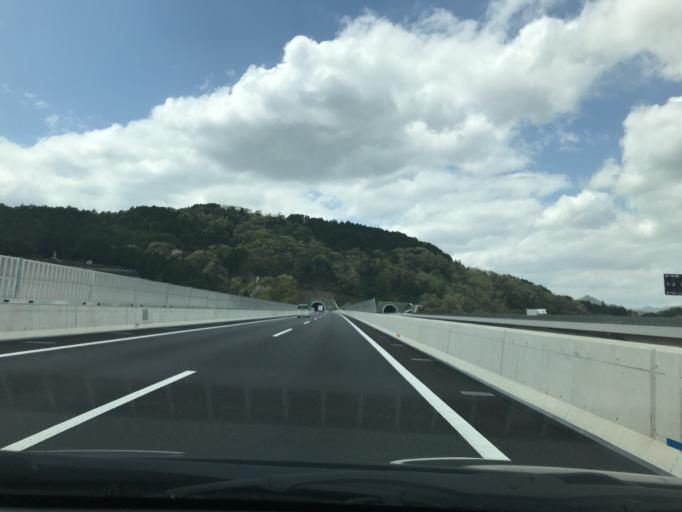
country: JP
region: Hyogo
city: Kawanishi
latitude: 34.8875
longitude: 135.3870
